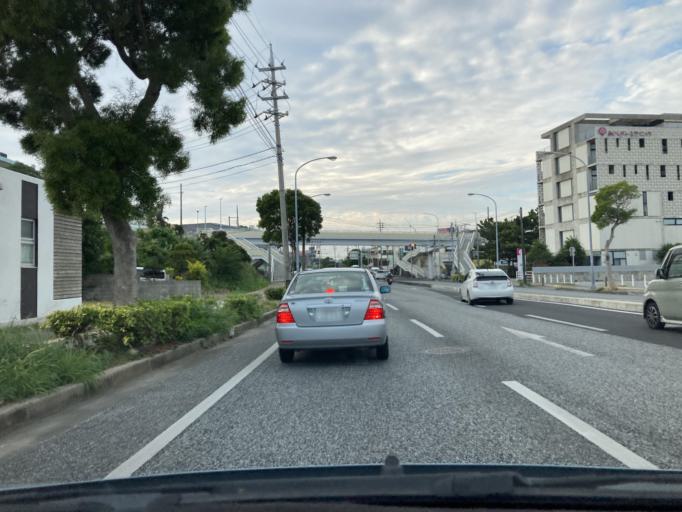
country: JP
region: Okinawa
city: Okinawa
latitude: 26.3526
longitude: 127.8139
